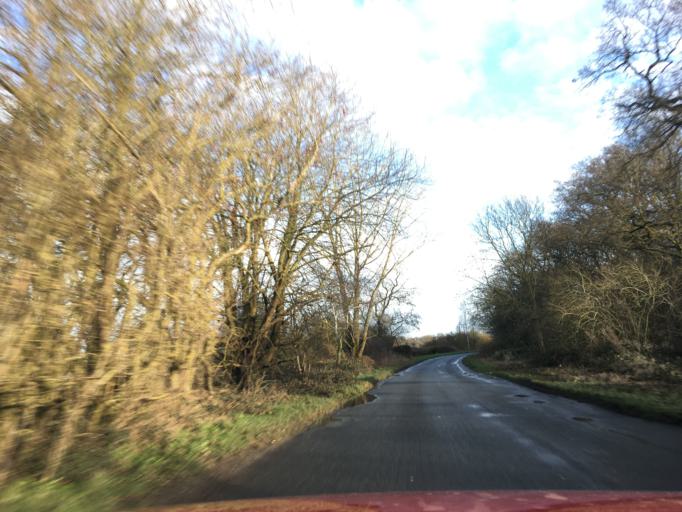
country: GB
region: England
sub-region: Warwickshire
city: Henley in Arden
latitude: 52.2234
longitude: -1.7950
